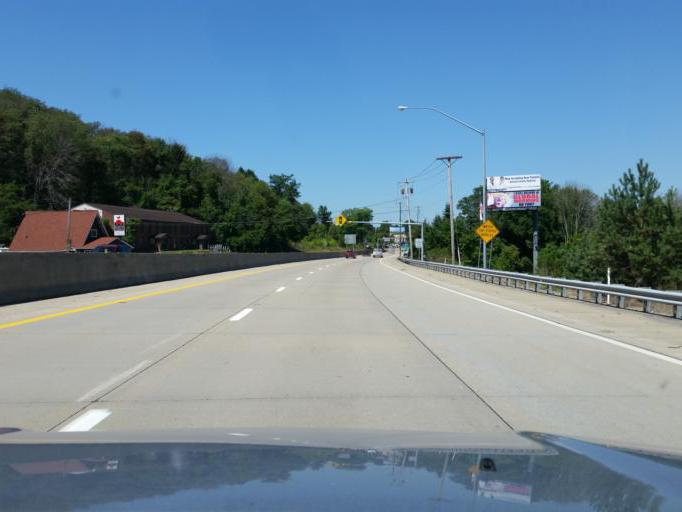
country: US
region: Pennsylvania
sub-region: Westmoreland County
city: Delmont
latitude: 40.3986
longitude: -79.5752
